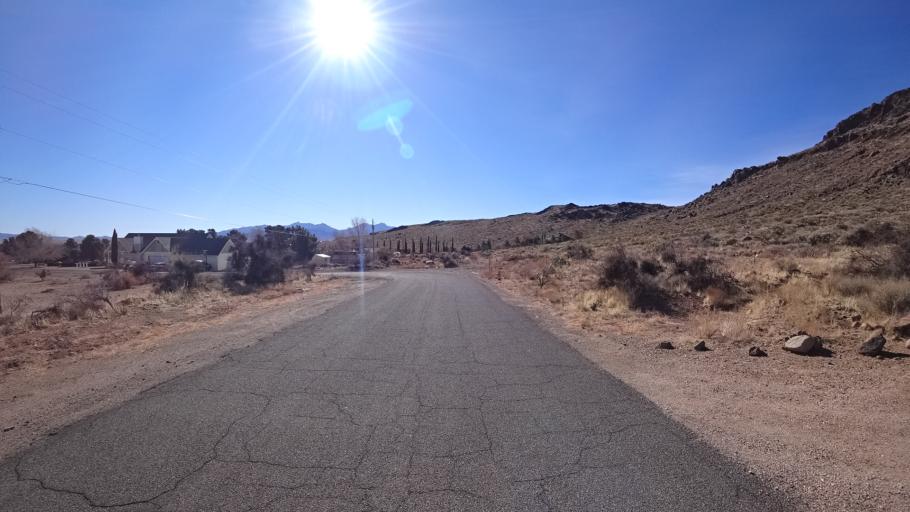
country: US
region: Arizona
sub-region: Mohave County
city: New Kingman-Butler
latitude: 35.2614
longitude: -114.0468
